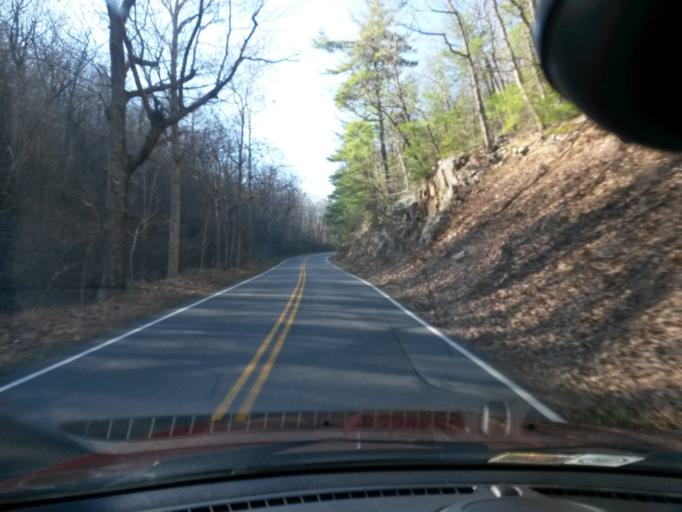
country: US
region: Virginia
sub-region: Botetourt County
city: Buchanan
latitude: 37.4909
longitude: -79.6619
